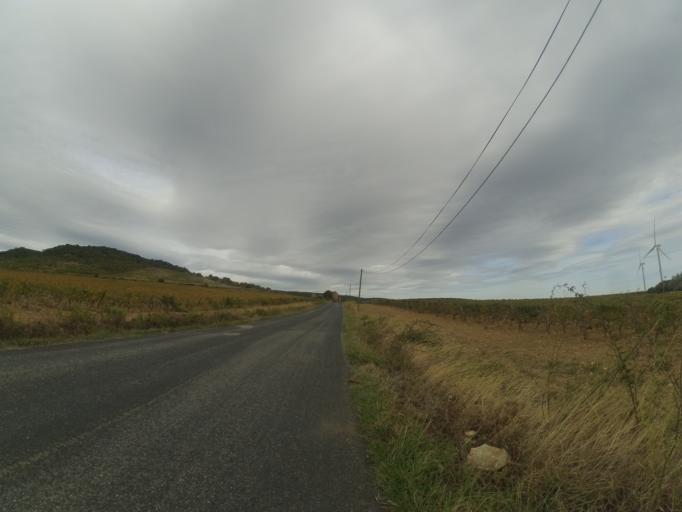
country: FR
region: Languedoc-Roussillon
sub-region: Departement des Pyrenees-Orientales
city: Corneilla-la-Riviere
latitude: 42.7233
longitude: 2.7403
